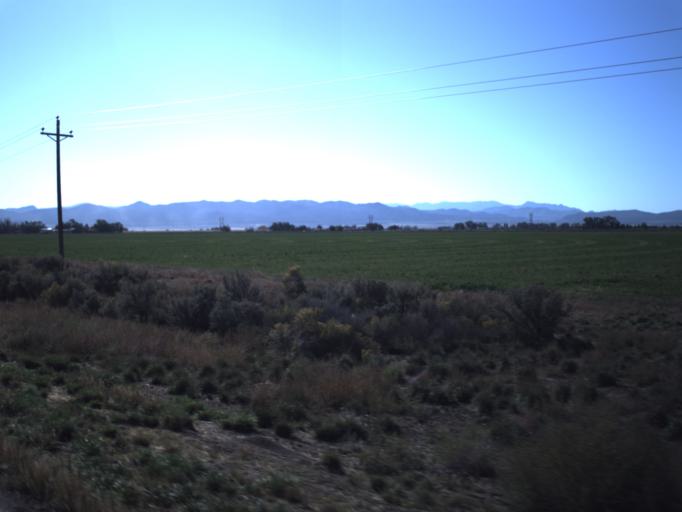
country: US
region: Utah
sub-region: Washington County
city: Enterprise
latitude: 37.7145
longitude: -113.6701
